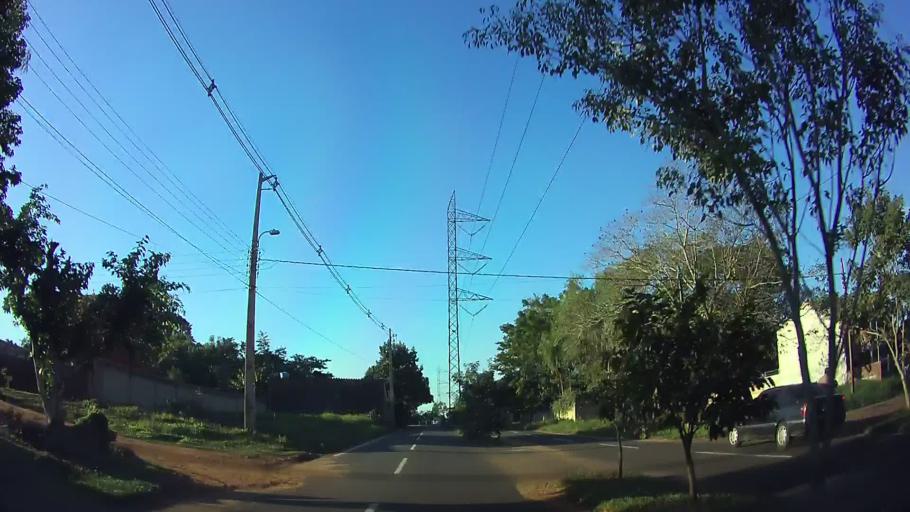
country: PY
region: Central
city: San Lorenzo
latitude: -25.2782
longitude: -57.4642
